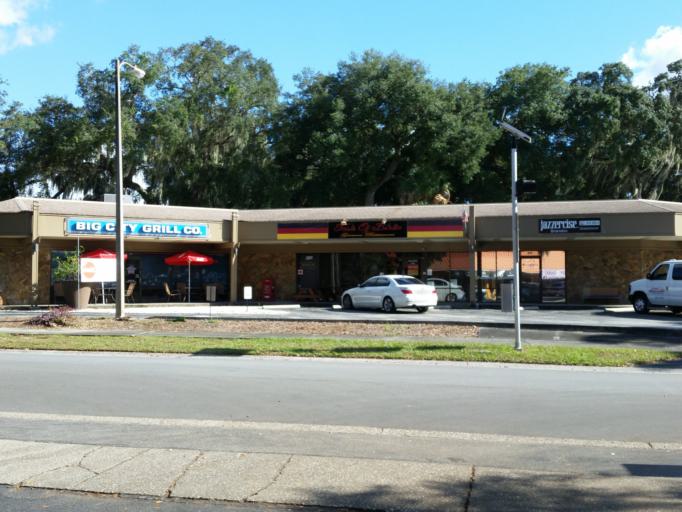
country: US
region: Florida
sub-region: Hillsborough County
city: Brandon
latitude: 27.9344
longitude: -82.2919
